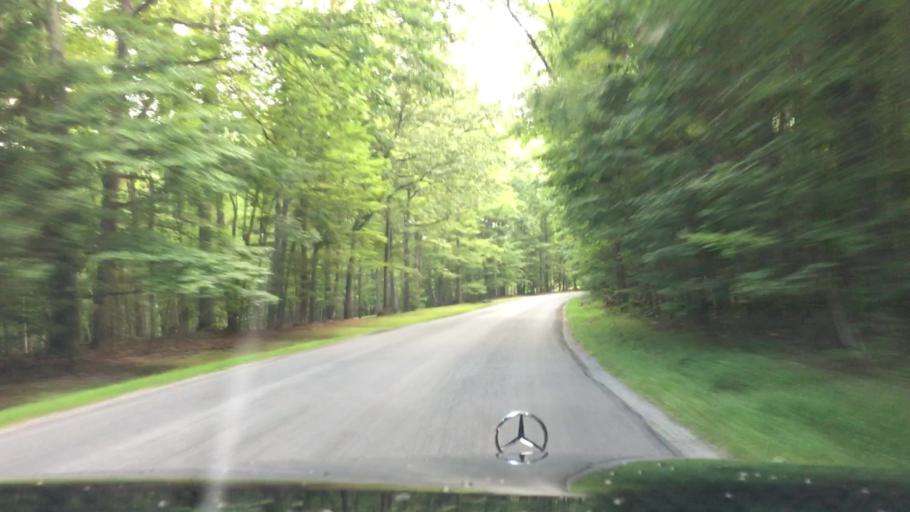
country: US
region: Virginia
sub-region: Campbell County
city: Timberlake
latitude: 37.2675
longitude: -79.3122
